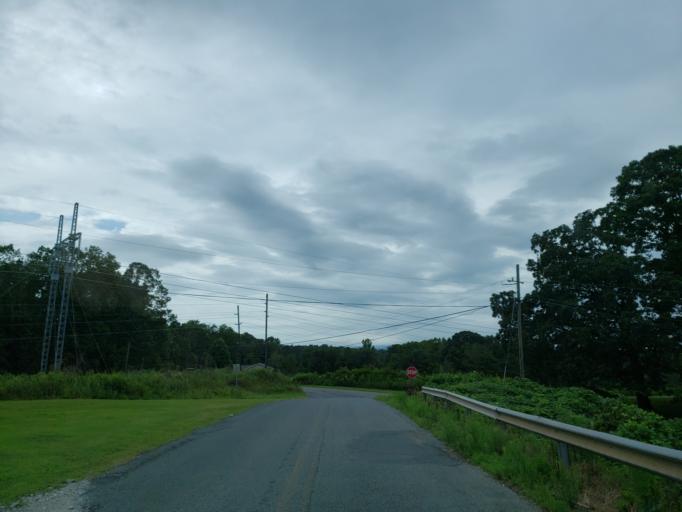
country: US
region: Georgia
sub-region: Gilmer County
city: Ellijay
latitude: 34.6418
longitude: -84.5015
